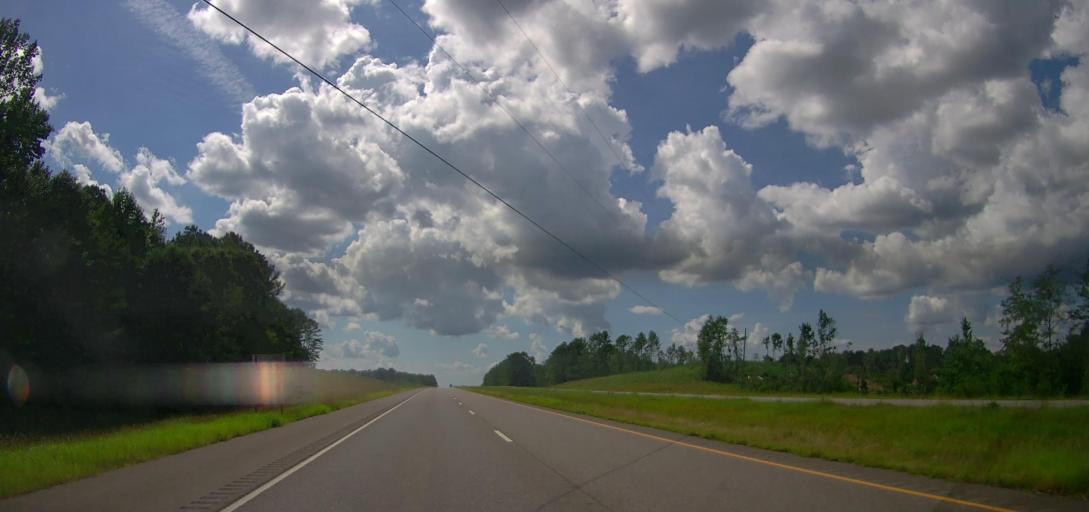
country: US
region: Alabama
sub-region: Pickens County
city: Reform
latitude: 33.3935
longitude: -88.0500
